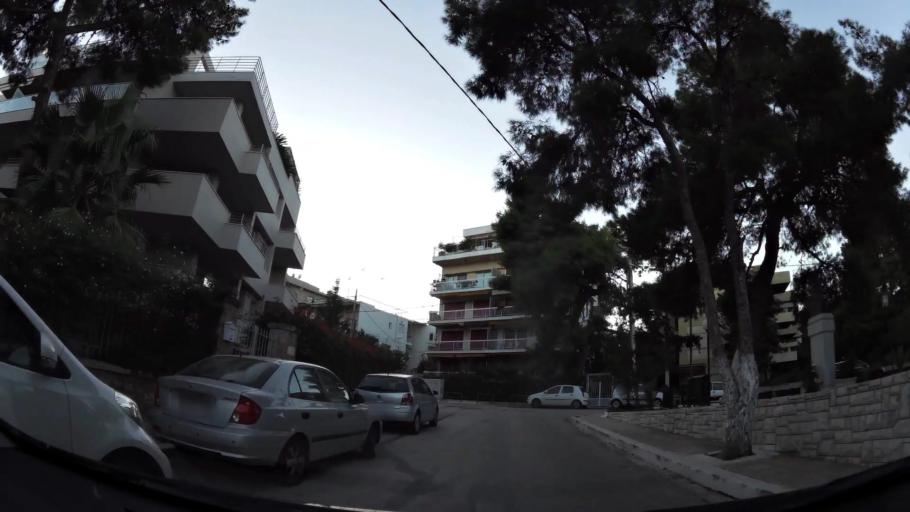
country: GR
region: Attica
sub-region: Nomarchia Anatolikis Attikis
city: Vari
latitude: 37.8157
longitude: 23.7998
